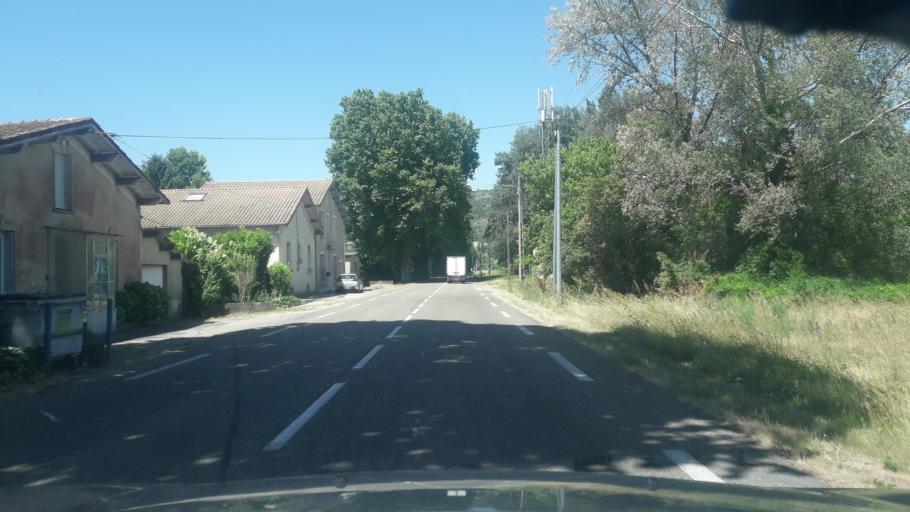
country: FR
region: Rhone-Alpes
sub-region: Departement de l'Ardeche
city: La Voulte-sur-Rhone
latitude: 44.7960
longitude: 4.7936
